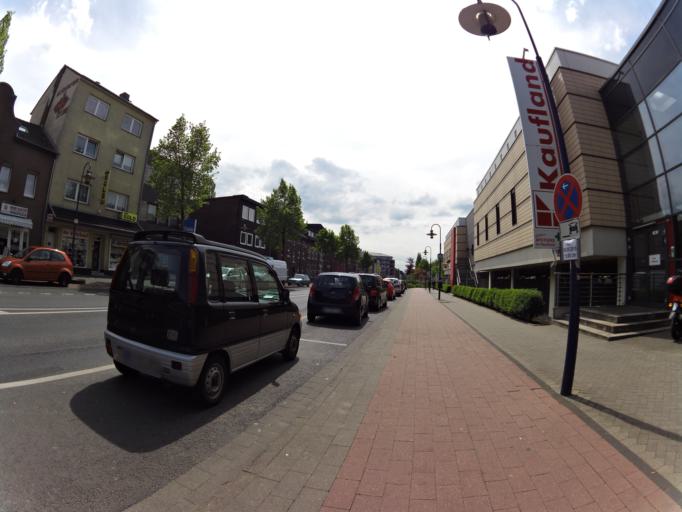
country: DE
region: North Rhine-Westphalia
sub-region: Regierungsbezirk Koln
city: Alsdorf
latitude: 50.8718
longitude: 6.1590
